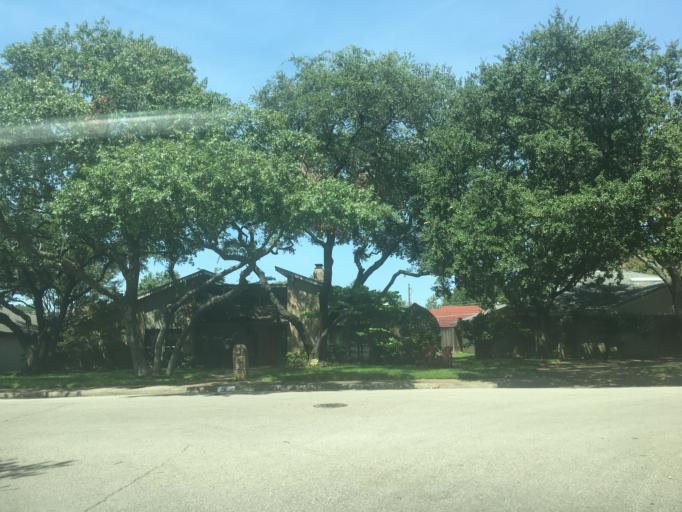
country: US
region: Texas
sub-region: Dallas County
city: University Park
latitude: 32.8753
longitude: -96.7398
